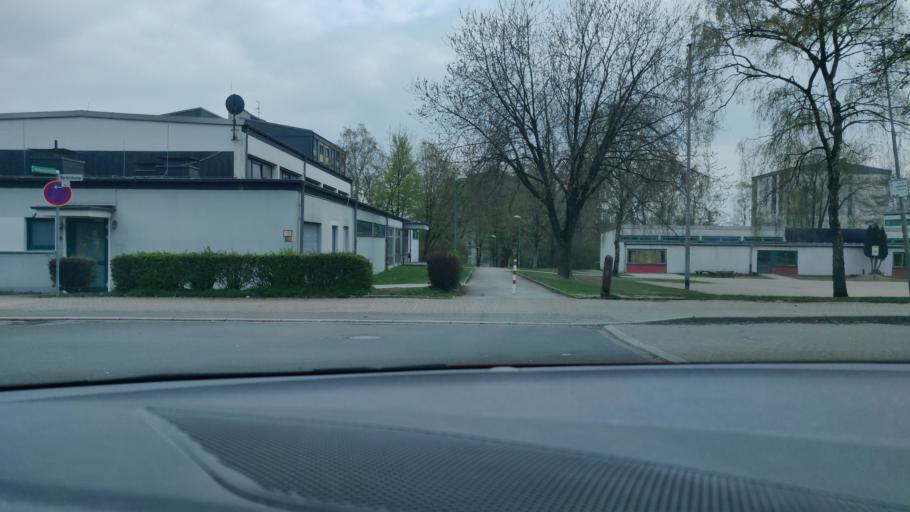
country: DE
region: North Rhine-Westphalia
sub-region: Regierungsbezirk Dusseldorf
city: Velbert
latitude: 51.3288
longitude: 7.0325
